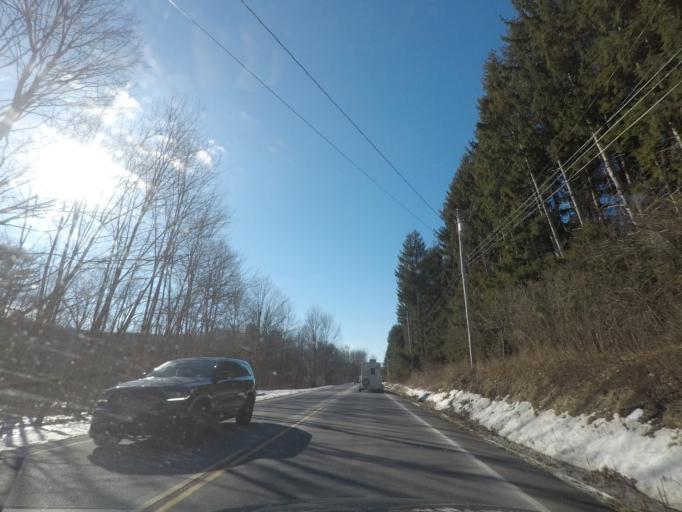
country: US
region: Massachusetts
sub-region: Berkshire County
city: Richmond
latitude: 42.4171
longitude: -73.4821
